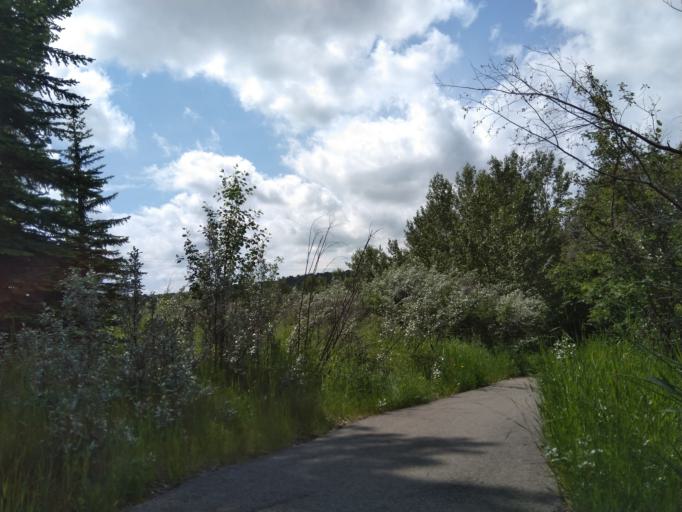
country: CA
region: Alberta
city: Cochrane
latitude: 51.1840
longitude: -114.4803
